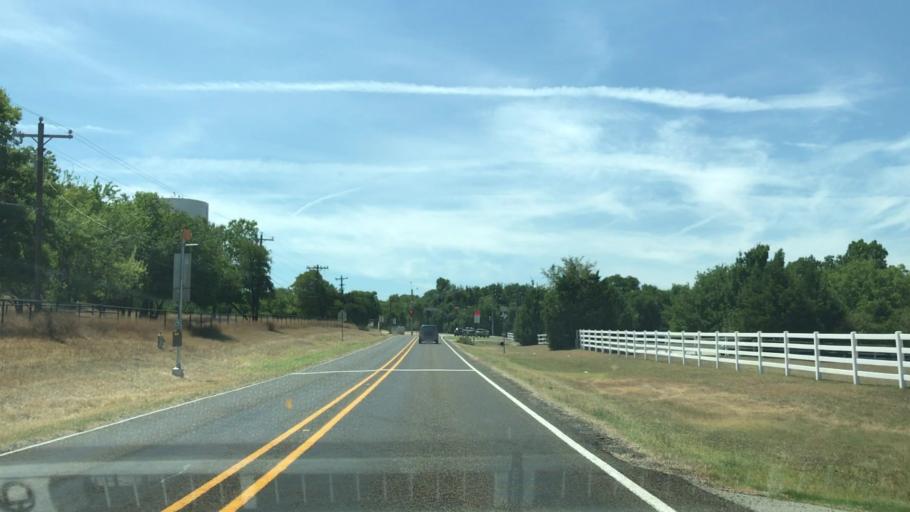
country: US
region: Texas
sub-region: Collin County
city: Fairview
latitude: 33.1334
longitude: -96.6095
